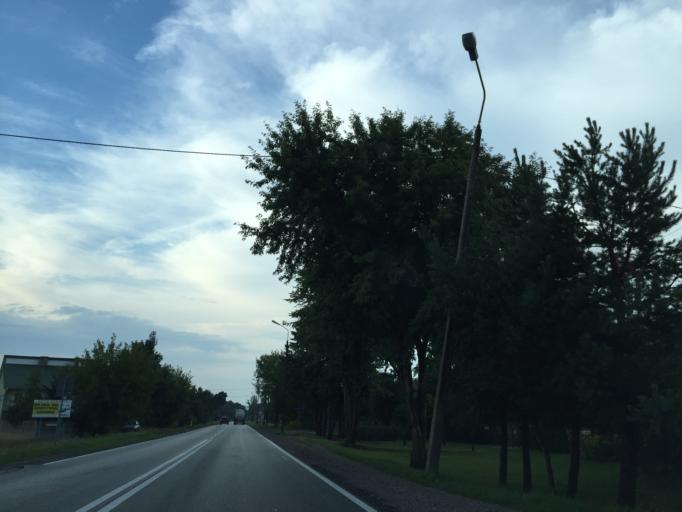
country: PL
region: Masovian Voivodeship
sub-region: Powiat wegrowski
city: Sadowne
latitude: 52.6349
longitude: 21.8448
